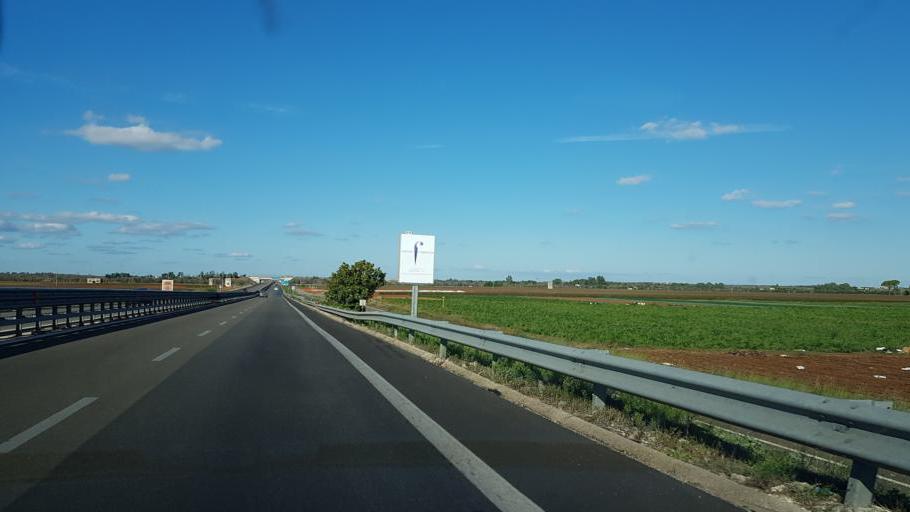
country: IT
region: Apulia
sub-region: Provincia di Lecce
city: Collemeto
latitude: 40.2498
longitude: 18.1152
